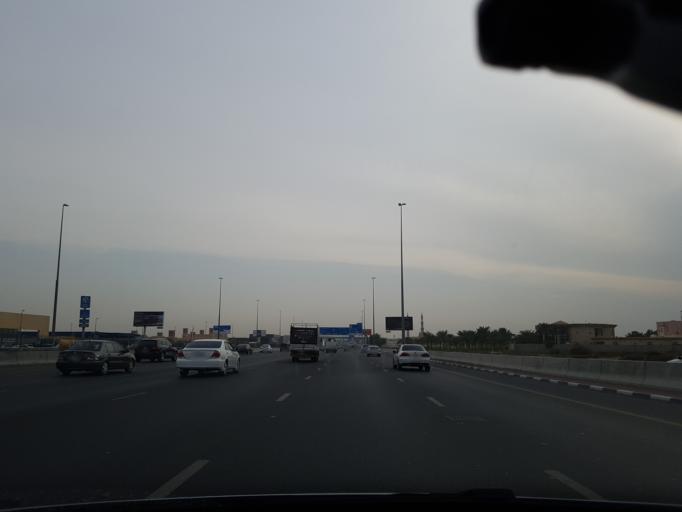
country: AE
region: Ash Shariqah
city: Sharjah
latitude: 25.3483
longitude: 55.4751
